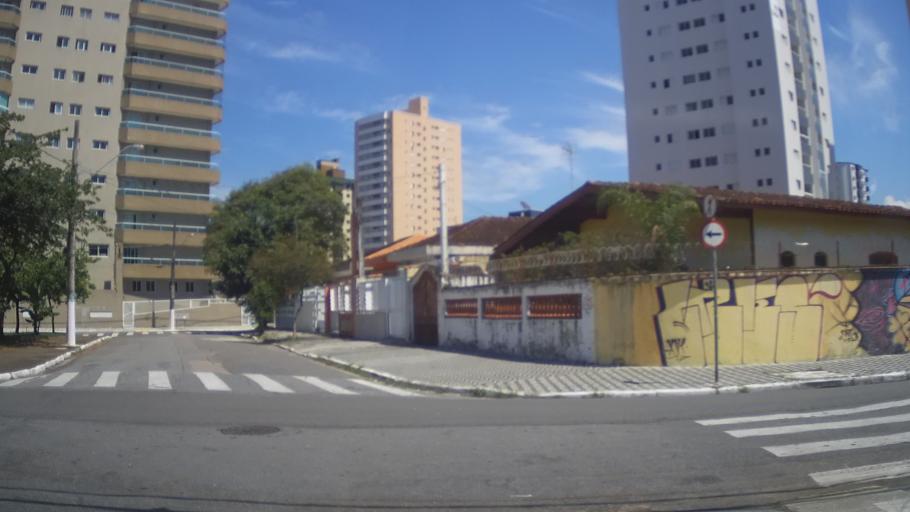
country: BR
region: Sao Paulo
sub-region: Praia Grande
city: Praia Grande
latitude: -24.0211
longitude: -46.4632
